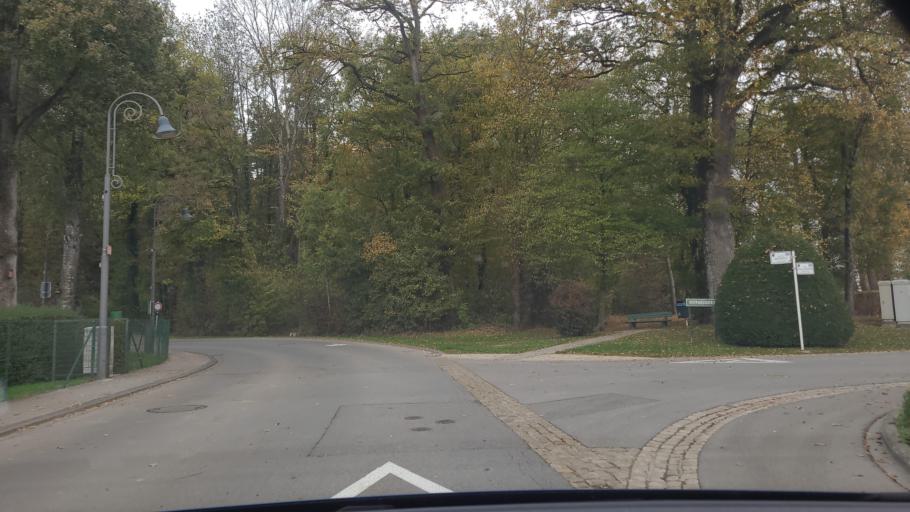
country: LU
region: Luxembourg
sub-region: Canton de Capellen
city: Kopstal
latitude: 49.6950
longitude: 6.0664
